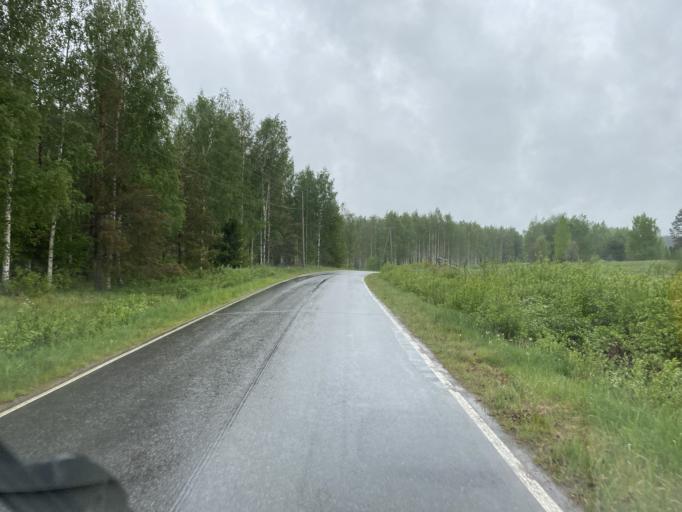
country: FI
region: Haeme
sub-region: Forssa
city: Humppila
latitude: 61.0662
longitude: 23.3221
